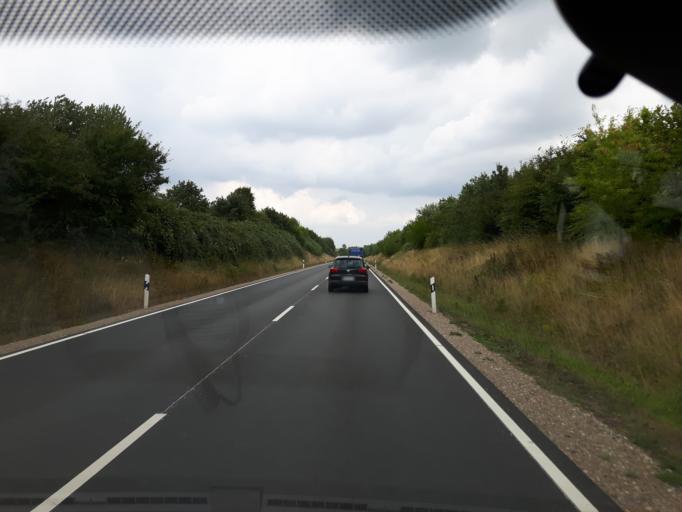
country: DE
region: Schleswig-Holstein
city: Gross Wittensee
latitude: 54.4077
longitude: 9.7599
